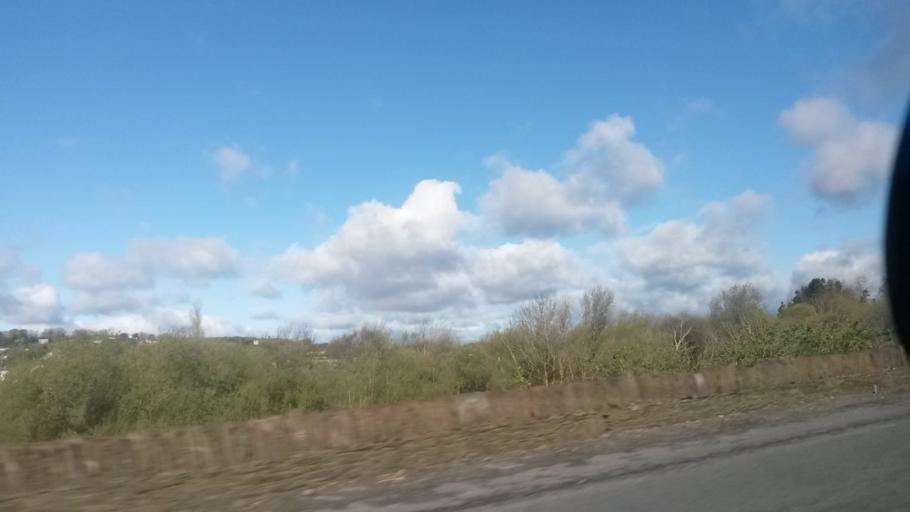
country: IE
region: Munster
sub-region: County Cork
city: Passage West
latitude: 51.8729
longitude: -8.3234
